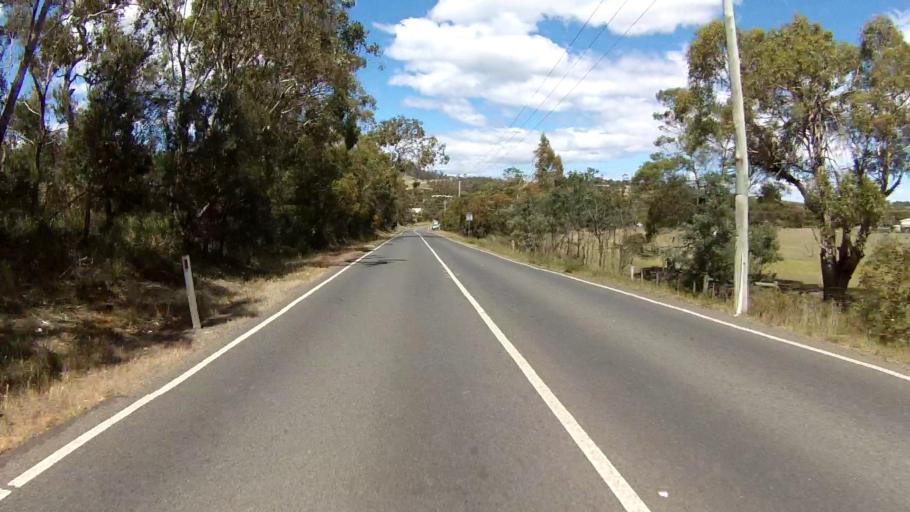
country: AU
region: Tasmania
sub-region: Clarence
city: Acton Park
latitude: -42.8641
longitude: 147.4795
